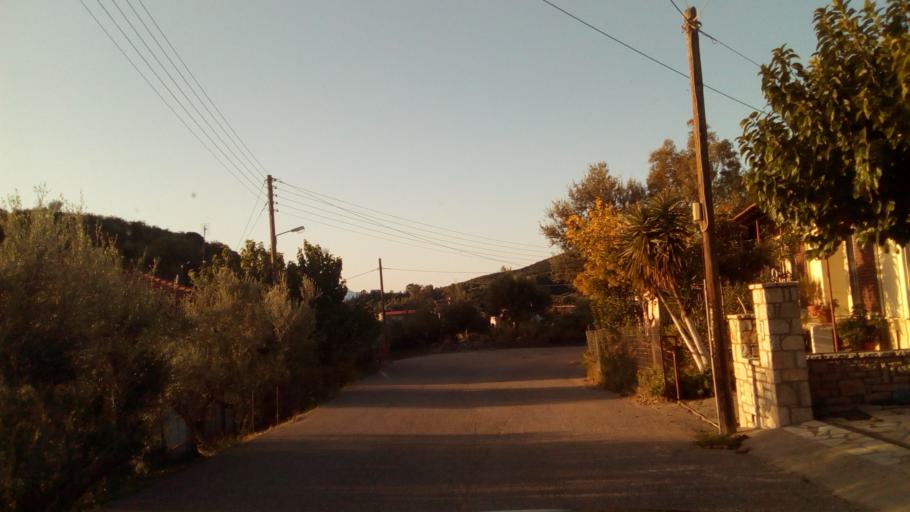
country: GR
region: West Greece
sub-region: Nomos Aitolias kai Akarnanias
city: Nafpaktos
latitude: 38.4017
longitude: 21.7961
